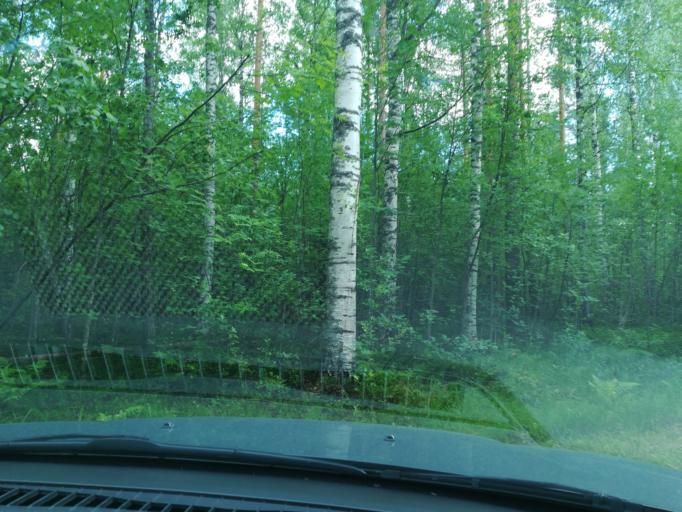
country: FI
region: Southern Savonia
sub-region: Mikkeli
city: Hirvensalmi
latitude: 61.6520
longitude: 26.7797
